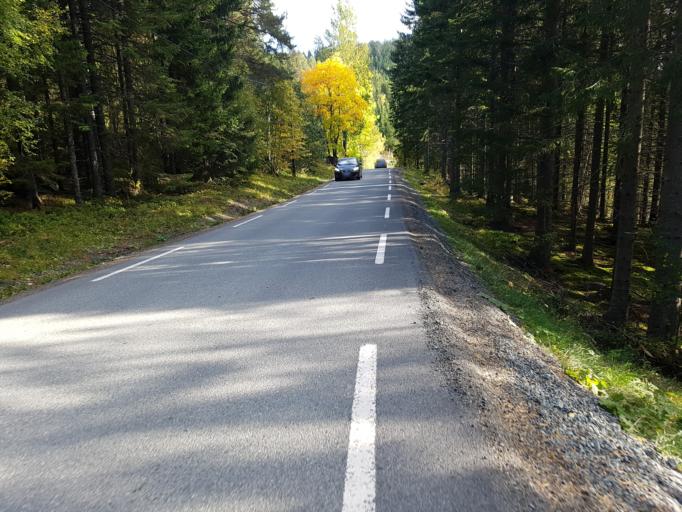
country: NO
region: Sor-Trondelag
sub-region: Malvik
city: Malvik
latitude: 63.3579
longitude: 10.6362
